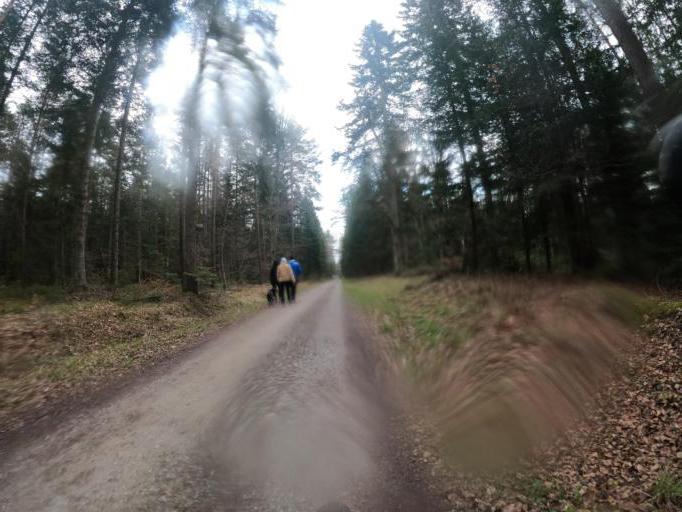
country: DE
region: Baden-Wuerttemberg
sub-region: Karlsruhe Region
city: Oberreichenbach
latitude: 48.7481
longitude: 8.6470
